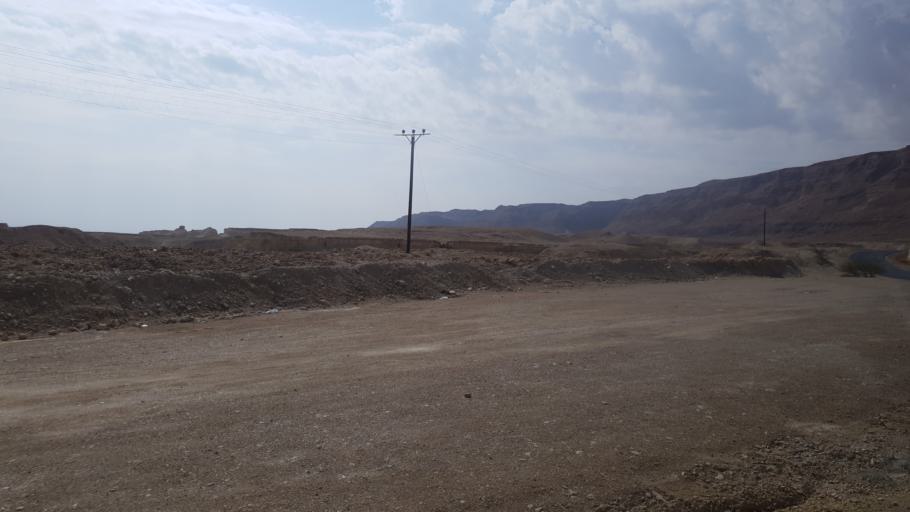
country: IL
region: Southern District
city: `En Boqeq
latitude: 31.3179
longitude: 35.3750
